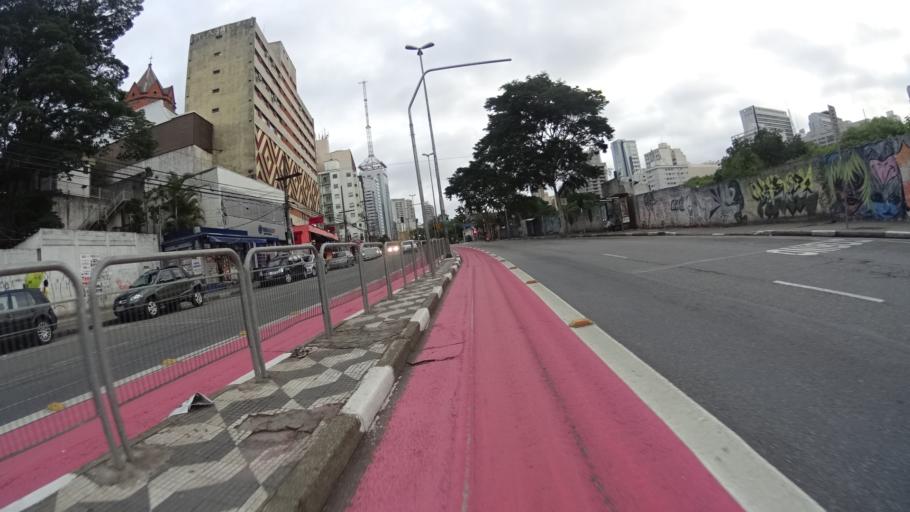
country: BR
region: Sao Paulo
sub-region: Sao Paulo
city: Sao Paulo
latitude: -23.5679
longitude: -46.6399
